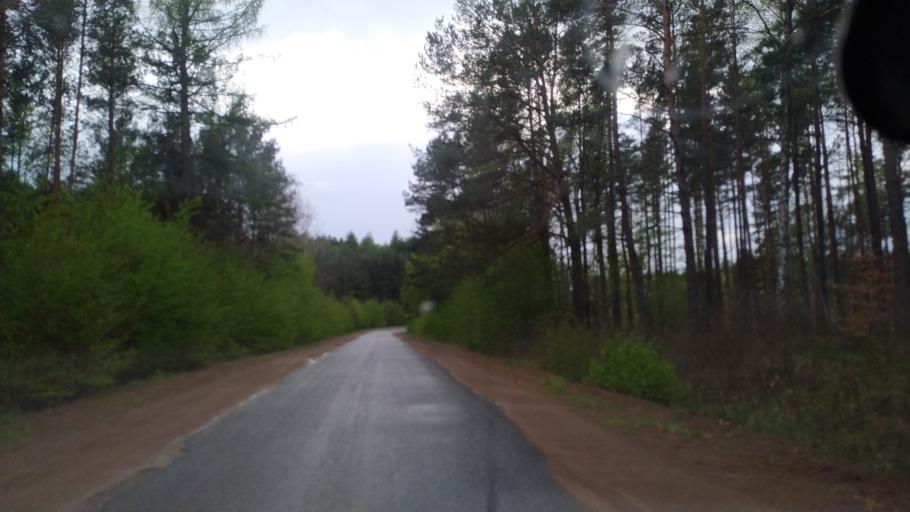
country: PL
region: Pomeranian Voivodeship
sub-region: Powiat starogardzki
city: Osiek
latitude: 53.6952
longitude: 18.5542
